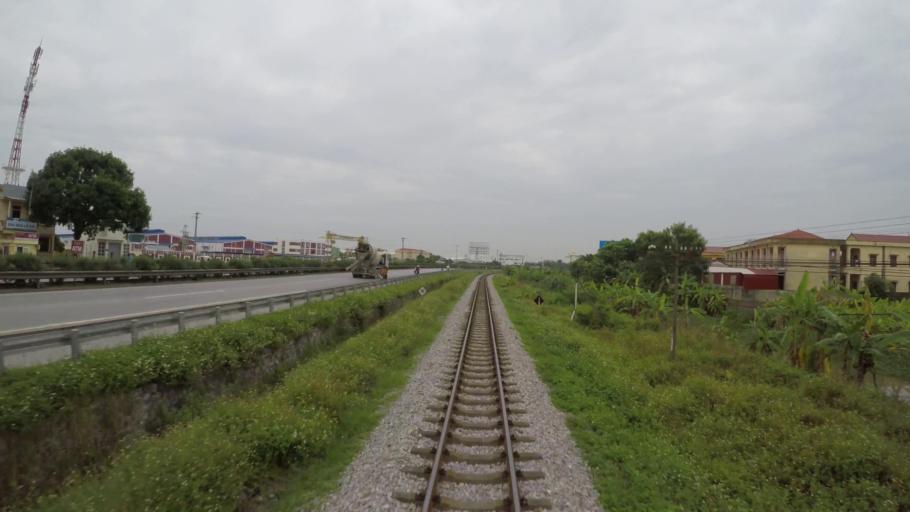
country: VN
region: Hai Duong
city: Nam Sach
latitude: 20.9781
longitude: 106.4139
